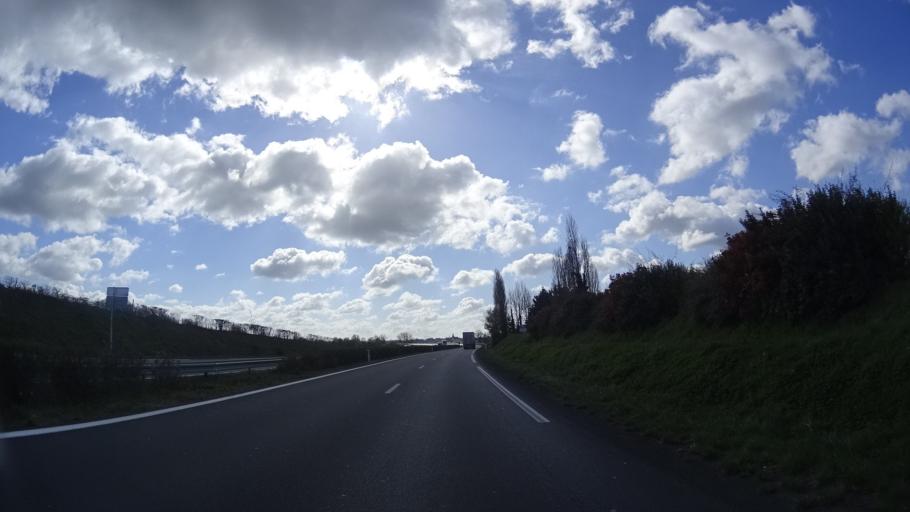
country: FR
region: Pays de la Loire
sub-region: Departement de Maine-et-Loire
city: Brissac-Quince
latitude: 47.3705
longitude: -0.4594
